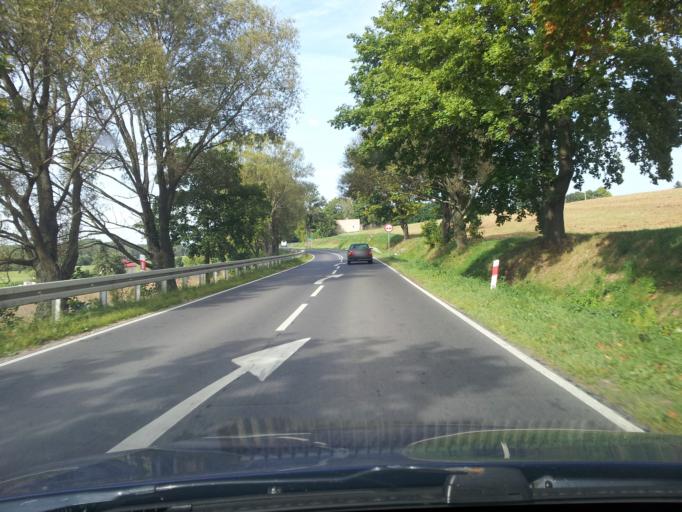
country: PL
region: Kujawsko-Pomorskie
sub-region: Powiat rypinski
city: Rypin
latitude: 53.1323
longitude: 19.3848
